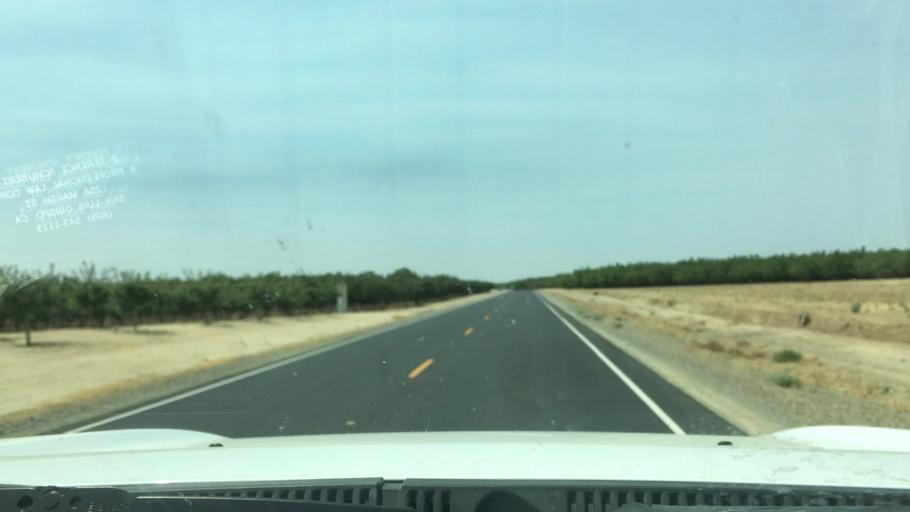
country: US
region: California
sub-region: Kern County
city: Lost Hills
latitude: 35.6105
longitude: -119.5840
